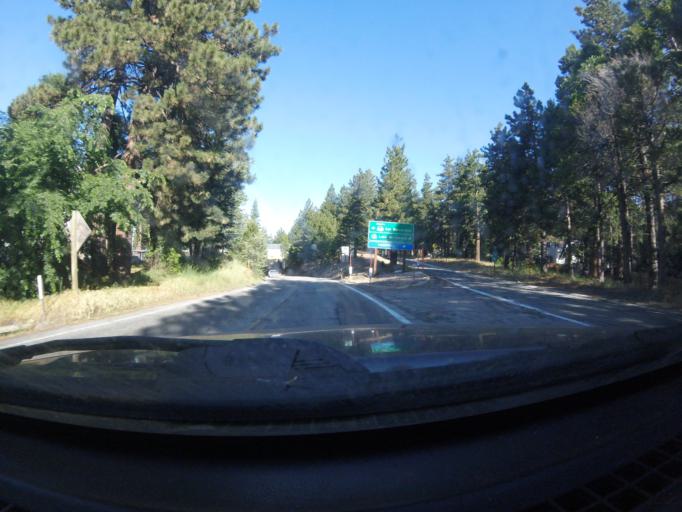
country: US
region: California
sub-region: San Bernardino County
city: Running Springs
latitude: 34.2055
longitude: -117.1069
